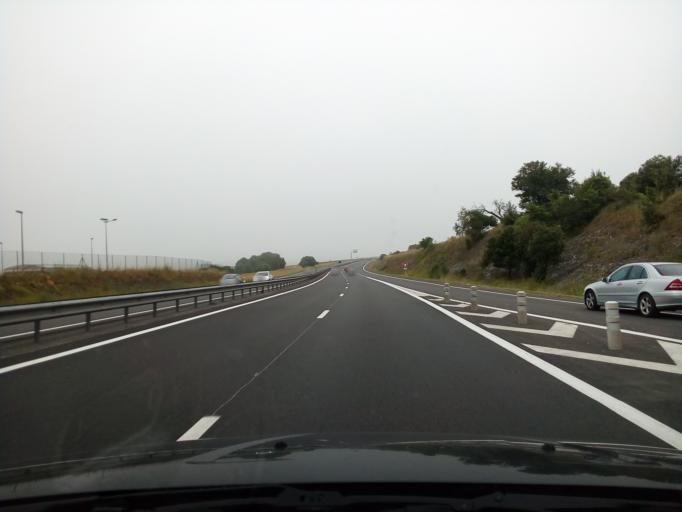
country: FR
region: Poitou-Charentes
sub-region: Departement de la Charente
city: Gensac-la-Pallue
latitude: 45.6650
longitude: -0.2339
